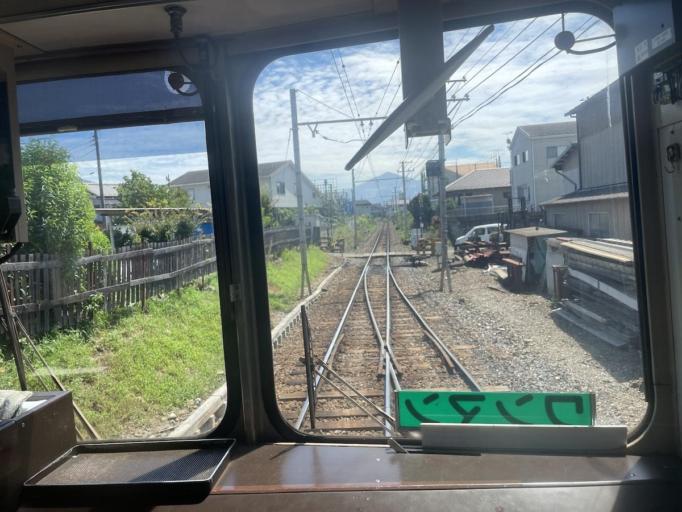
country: JP
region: Saitama
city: Chichibu
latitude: 36.0667
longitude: 139.0941
